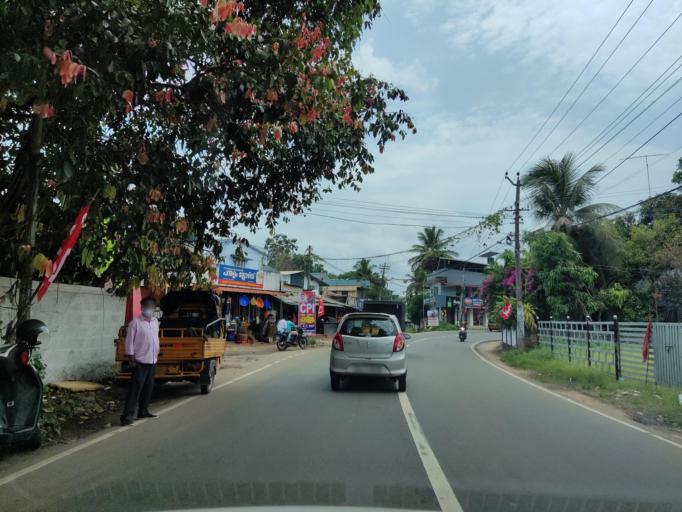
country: IN
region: Kerala
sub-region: Pattanamtitta
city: Adur
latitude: 9.2243
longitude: 76.6716
